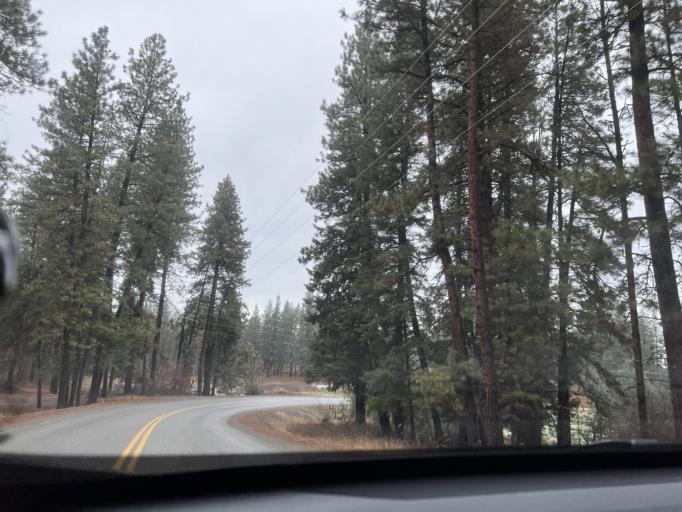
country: US
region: Washington
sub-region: Okanogan County
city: Brewster
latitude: 48.4661
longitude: -120.2081
